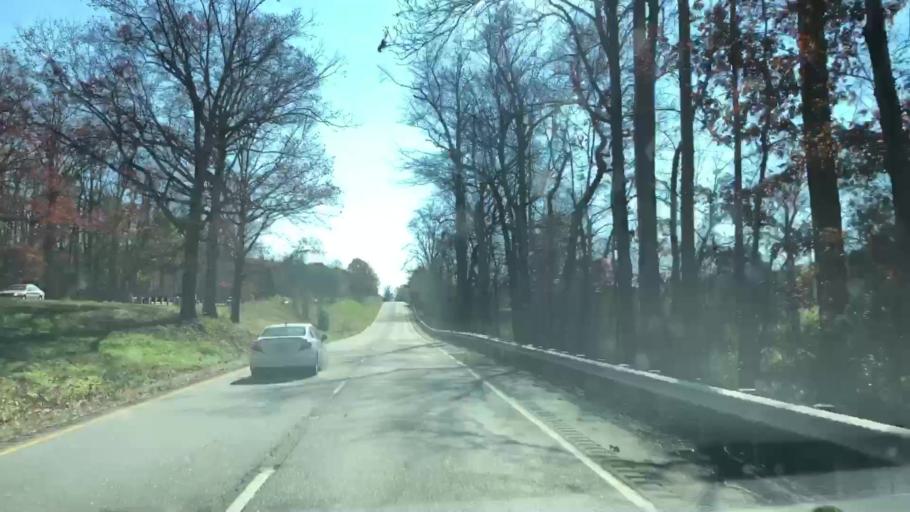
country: US
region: Virginia
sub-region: Greene County
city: Ruckersville
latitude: 38.2590
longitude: -78.3582
